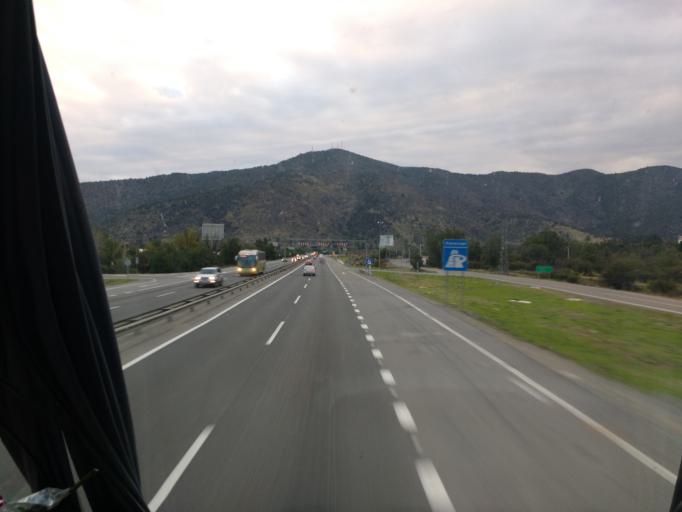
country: CL
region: Santiago Metropolitan
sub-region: Provincia de Talagante
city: Penaflor
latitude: -33.4575
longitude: -70.9201
